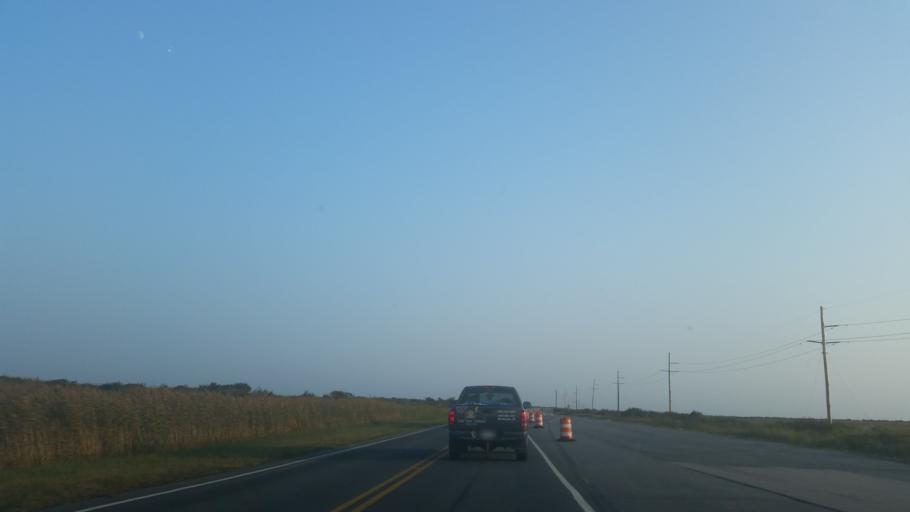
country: US
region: North Carolina
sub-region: Dare County
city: Wanchese
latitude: 35.6743
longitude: -75.4804
